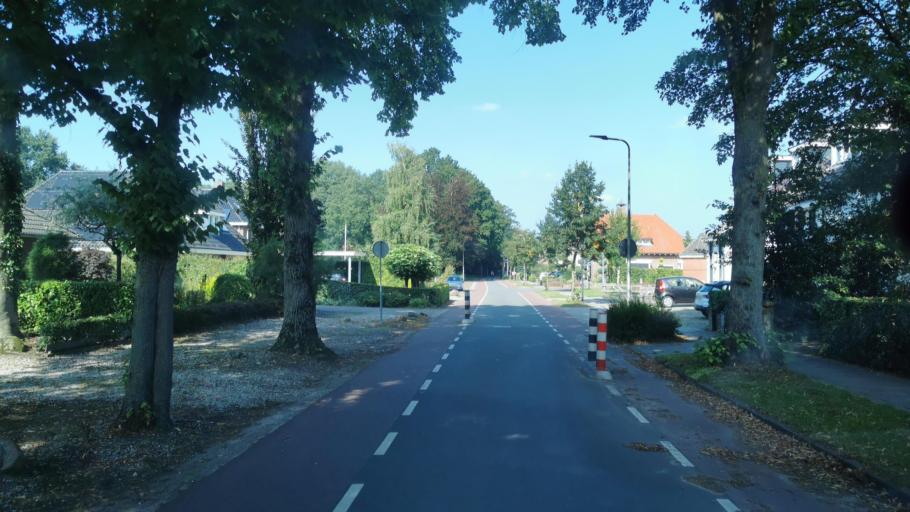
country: NL
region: Overijssel
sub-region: Gemeente Oldenzaal
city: Oldenzaal
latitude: 52.3531
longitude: 6.9221
